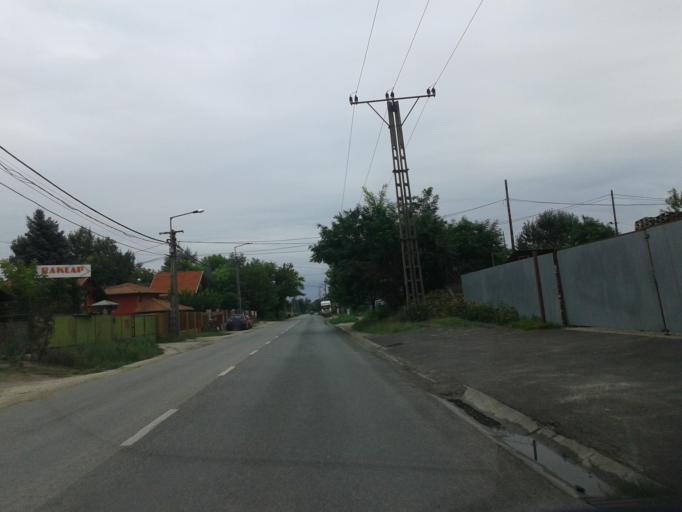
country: HU
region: Pest
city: Szigethalom
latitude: 47.3204
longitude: 19.0173
